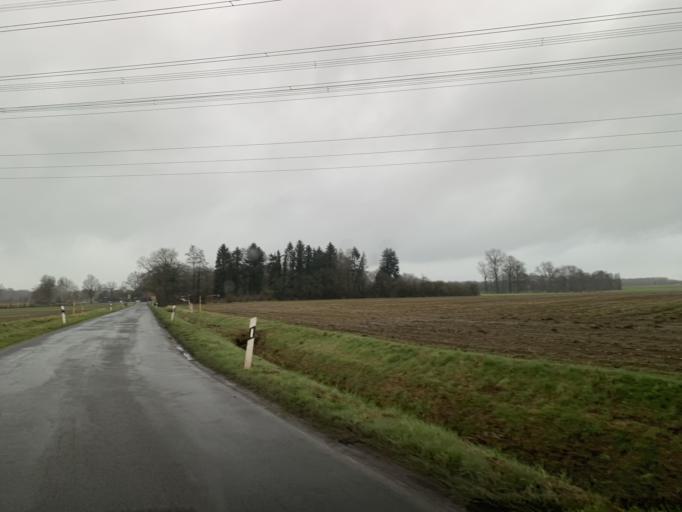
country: DE
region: North Rhine-Westphalia
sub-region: Regierungsbezirk Munster
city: Havixbeck
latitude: 51.9653
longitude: 7.4658
